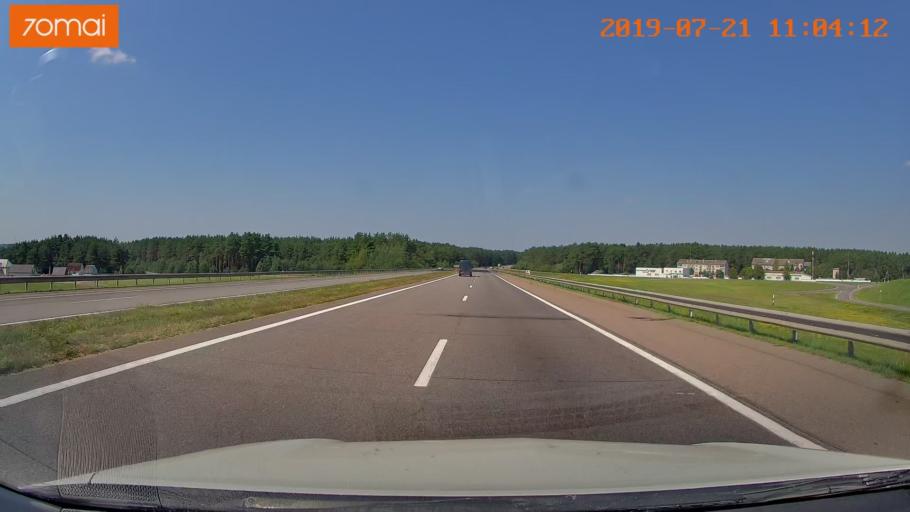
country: BY
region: Minsk
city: Rakaw
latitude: 53.9784
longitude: 27.0446
